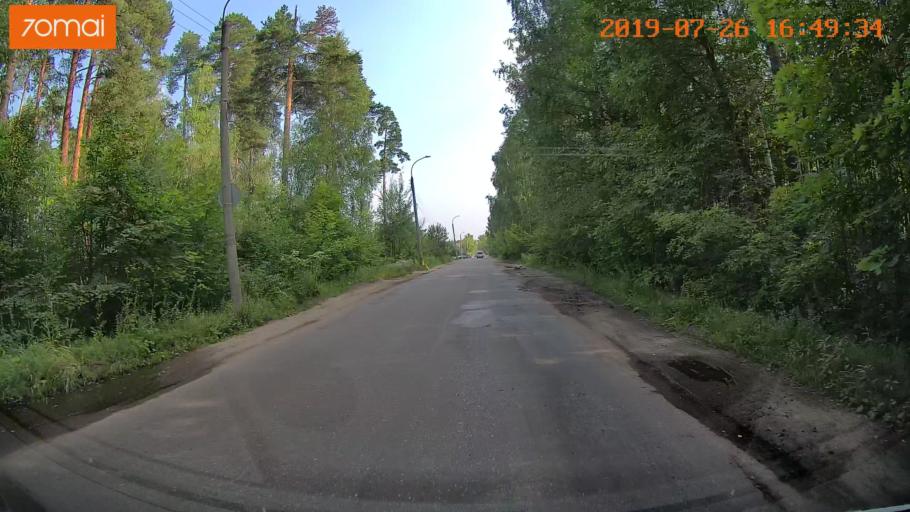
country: RU
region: Ivanovo
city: Bogorodskoye
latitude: 57.0285
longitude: 41.0207
